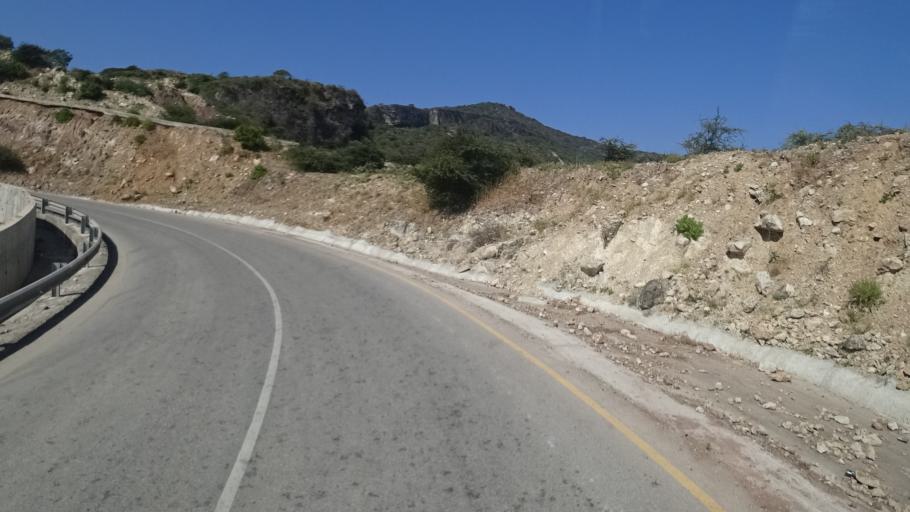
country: OM
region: Zufar
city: Salalah
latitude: 17.0528
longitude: 54.6124
